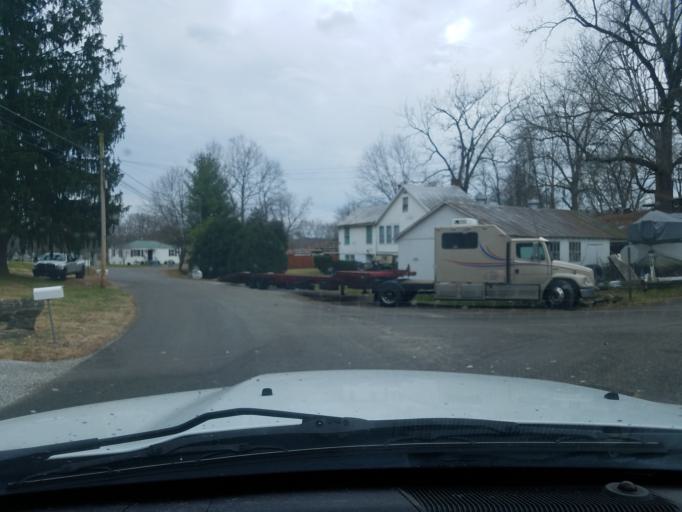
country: US
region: Kentucky
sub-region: Jefferson County
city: Prospect
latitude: 38.3377
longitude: -85.6531
